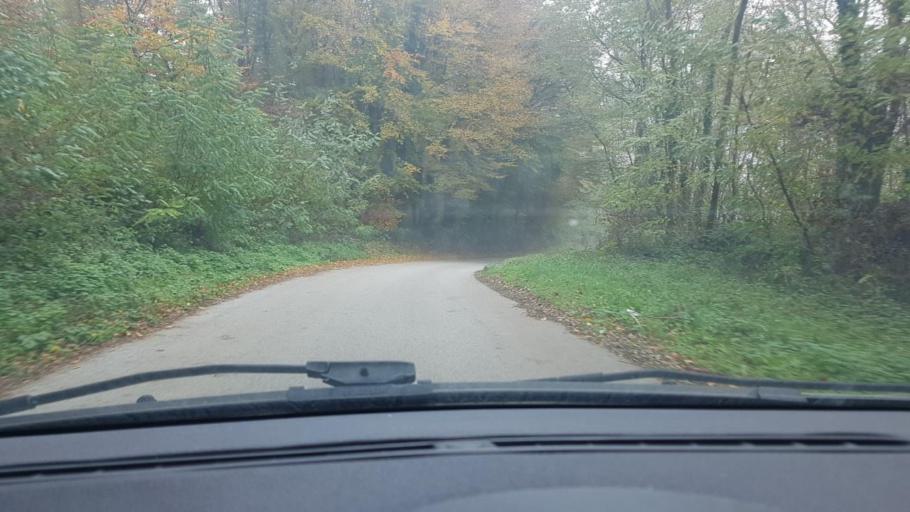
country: HR
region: Krapinsko-Zagorska
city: Mihovljan
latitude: 46.1451
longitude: 15.9784
